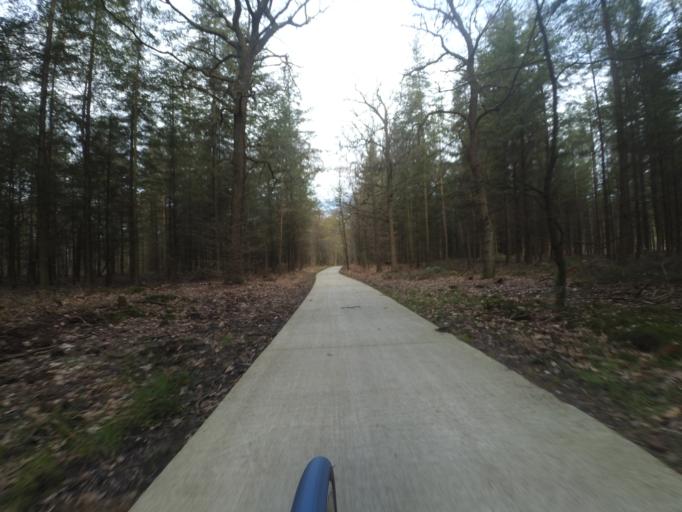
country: NL
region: Gelderland
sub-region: Gemeente Nunspeet
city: Nunspeet
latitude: 52.3424
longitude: 5.7826
